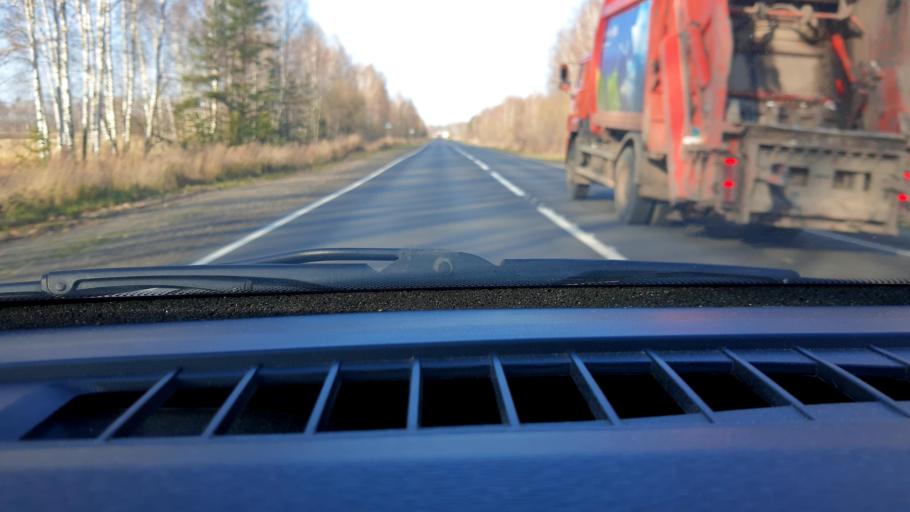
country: RU
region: Nizjnij Novgorod
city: Novaya Balakhna
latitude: 56.5698
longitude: 43.7120
